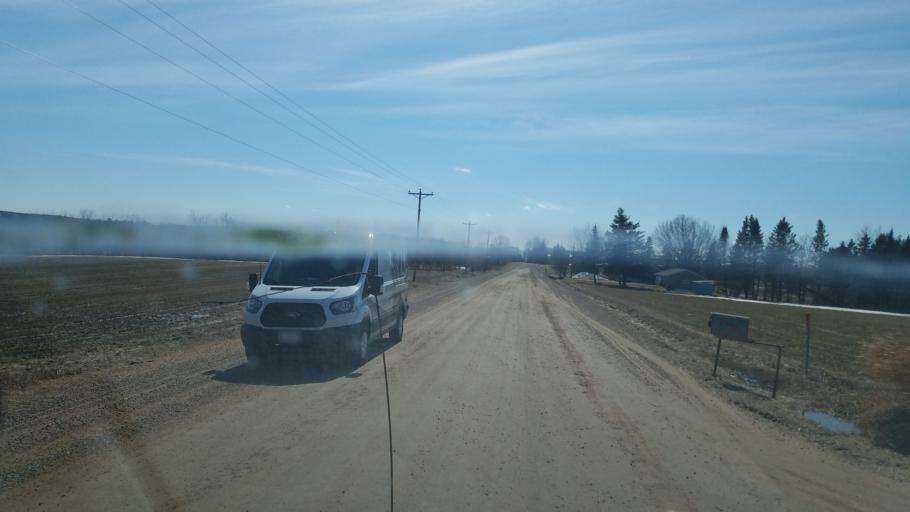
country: US
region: Wisconsin
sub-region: Clark County
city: Loyal
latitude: 44.6050
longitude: -90.4565
